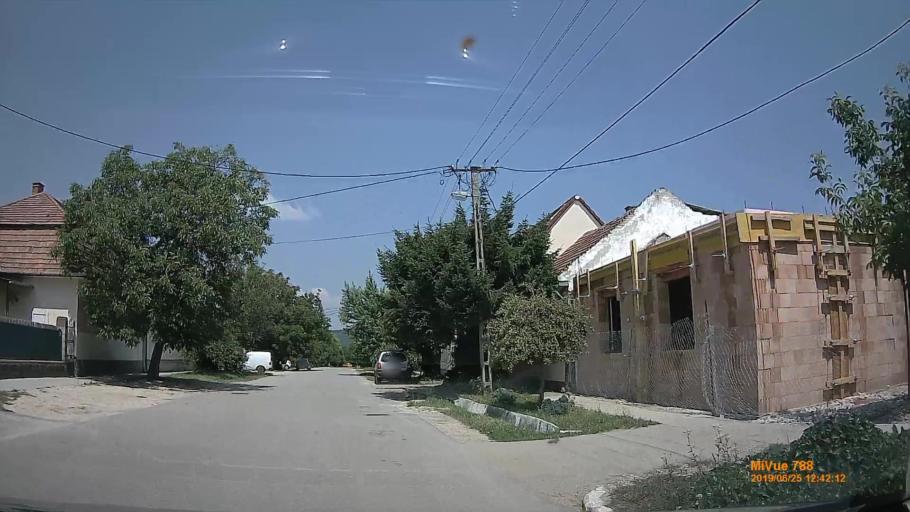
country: HU
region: Komarom-Esztergom
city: Esztergom
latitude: 47.8043
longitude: 18.7413
